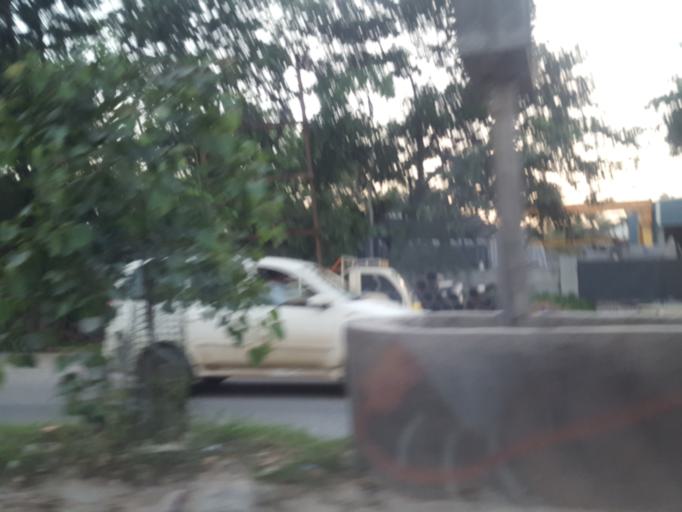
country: IN
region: Telangana
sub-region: Medak
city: Serilingampalle
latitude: 17.5218
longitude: 78.3565
